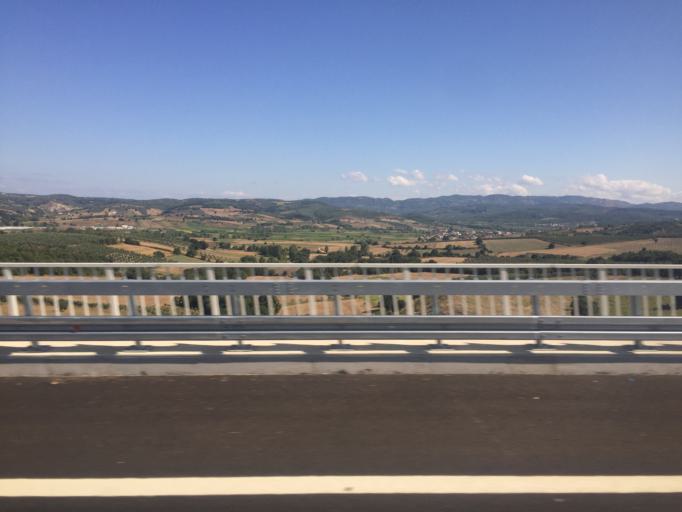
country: TR
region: Bursa
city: Gorukle
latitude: 40.2561
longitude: 28.7335
